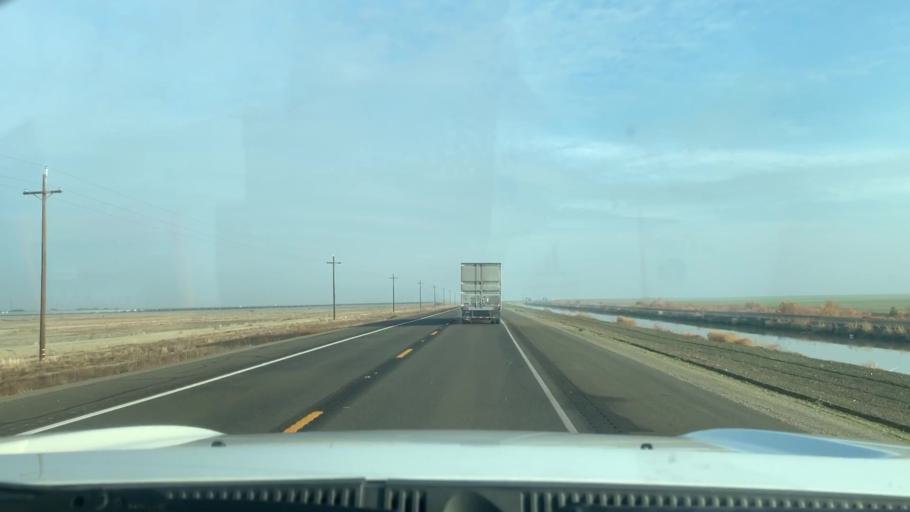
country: US
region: California
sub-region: Kings County
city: Kettleman City
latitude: 36.0538
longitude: -119.9431
